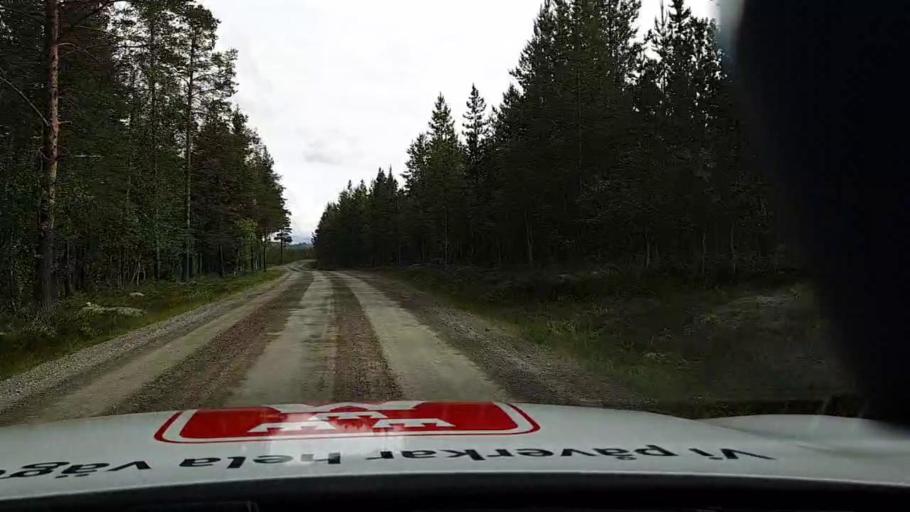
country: SE
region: Jaemtland
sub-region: Are Kommun
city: Jarpen
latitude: 62.4951
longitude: 13.5045
